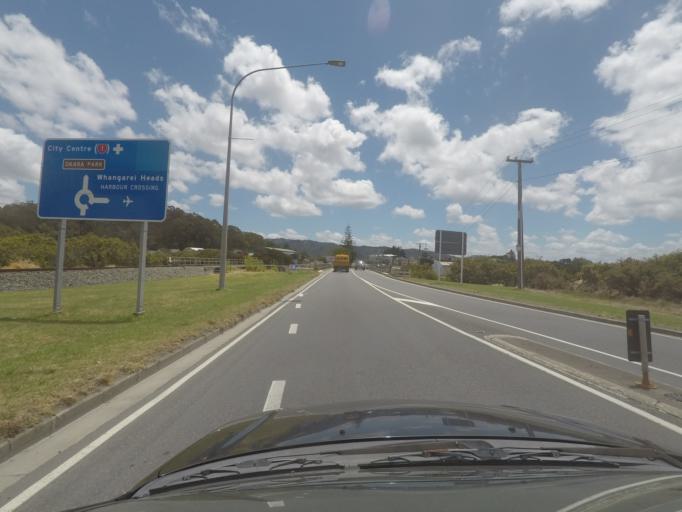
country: NZ
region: Northland
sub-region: Whangarei
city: Whangarei
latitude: -35.7384
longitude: 174.3341
